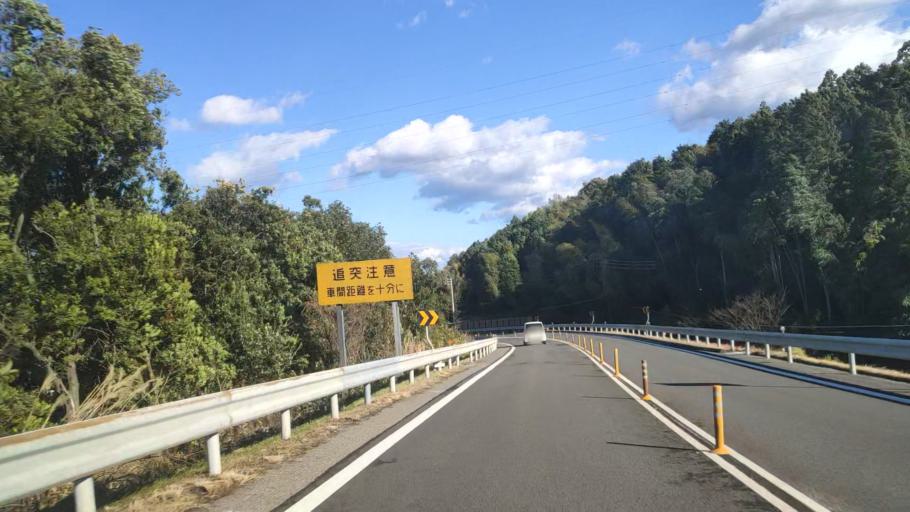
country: JP
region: Ehime
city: Saijo
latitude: 33.9173
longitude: 133.2389
